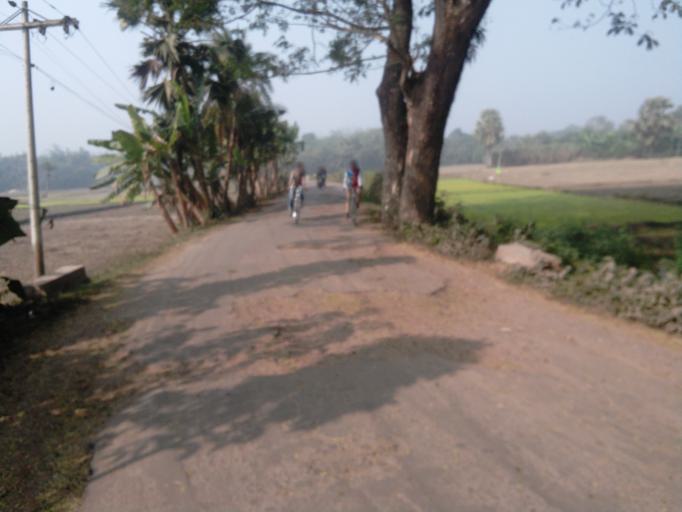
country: BD
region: Khulna
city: Kesabpur
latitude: 22.7501
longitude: 89.2446
